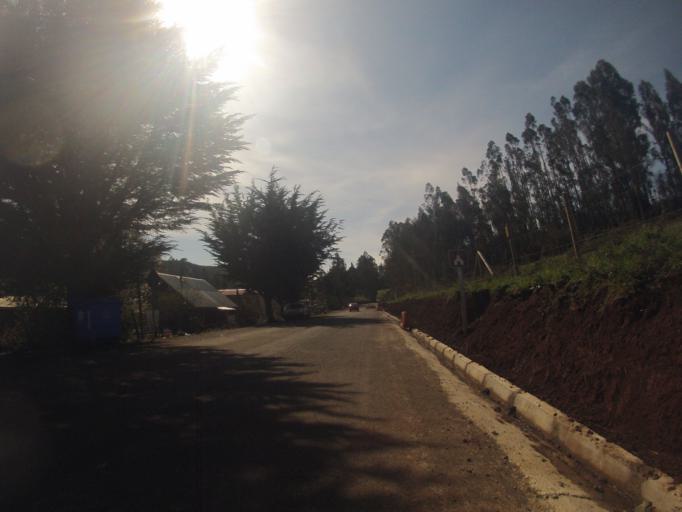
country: CL
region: Araucania
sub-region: Provincia de Cautin
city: Temuco
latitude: -38.6866
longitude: -72.5836
